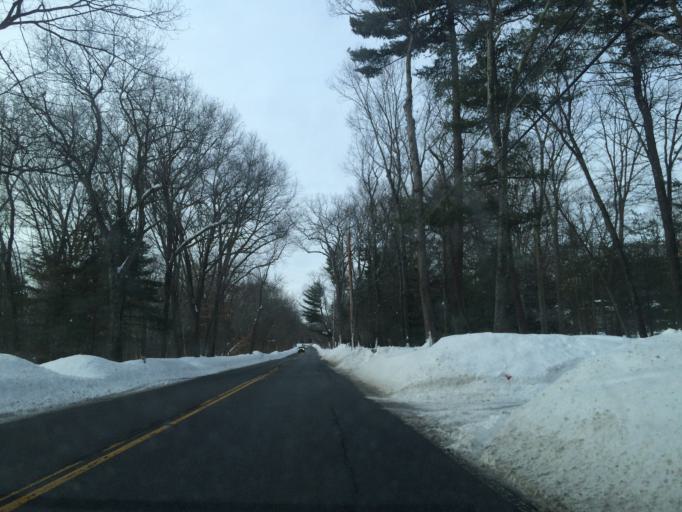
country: US
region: Massachusetts
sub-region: Middlesex County
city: Weston
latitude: 42.3387
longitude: -71.3165
